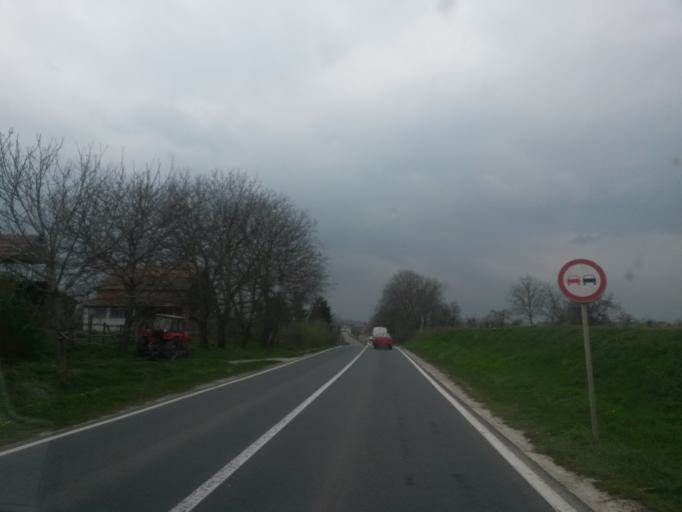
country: HR
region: Vukovarsko-Srijemska
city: Slakovci
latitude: 45.2126
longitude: 18.9920
